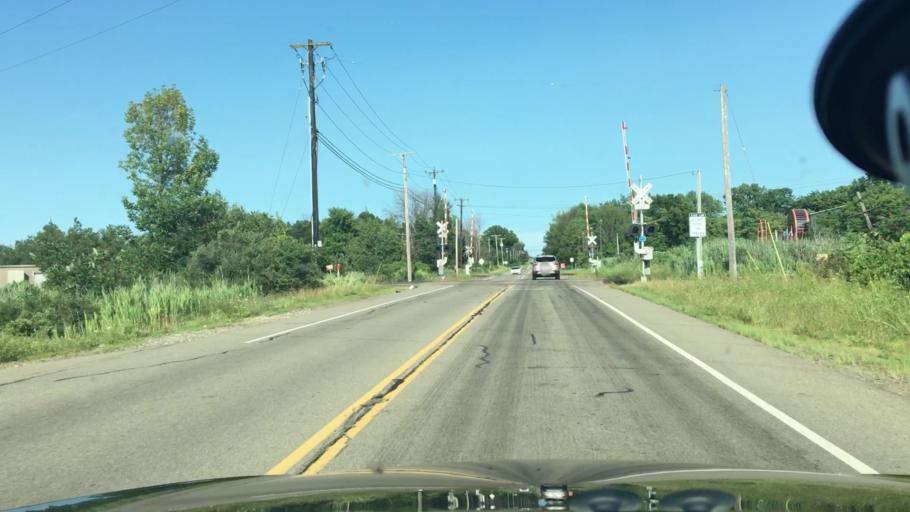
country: US
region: New York
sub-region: Erie County
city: Angola
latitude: 42.6525
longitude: -79.0116
